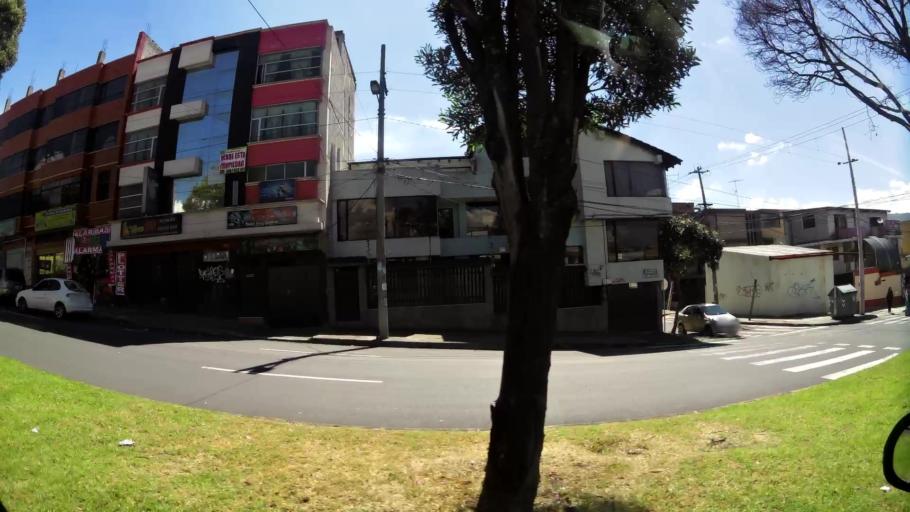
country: EC
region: Pichincha
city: Quito
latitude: -0.2502
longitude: -78.5349
